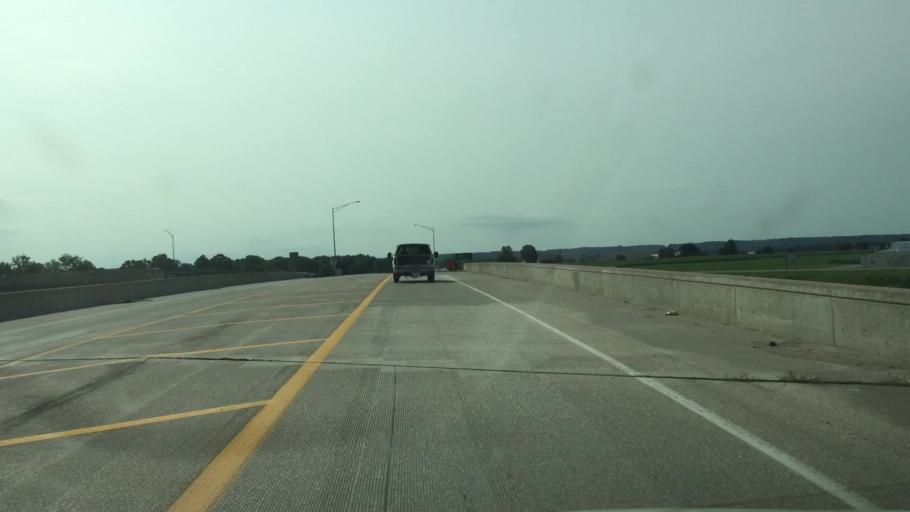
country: US
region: Illinois
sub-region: Hancock County
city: Nauvoo
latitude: 40.6264
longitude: -91.3994
